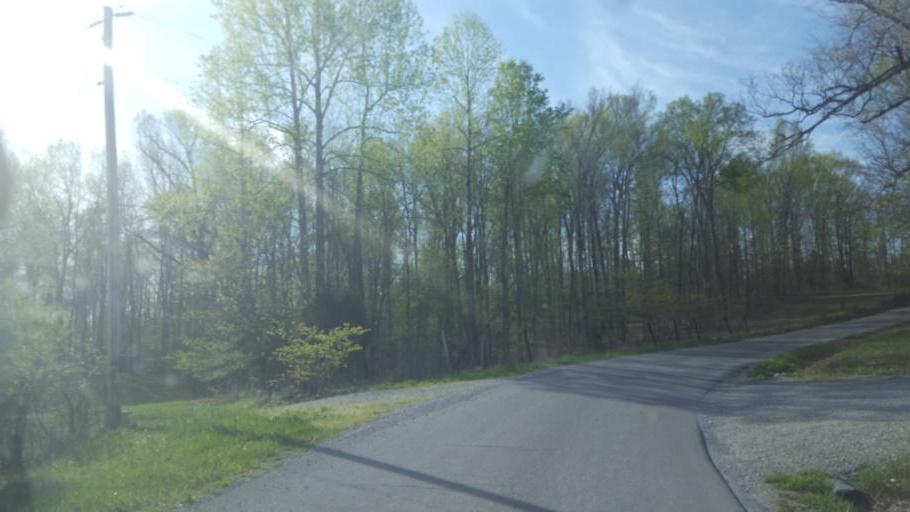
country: US
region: Kentucky
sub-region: Hart County
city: Munfordville
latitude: 37.3187
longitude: -86.0736
